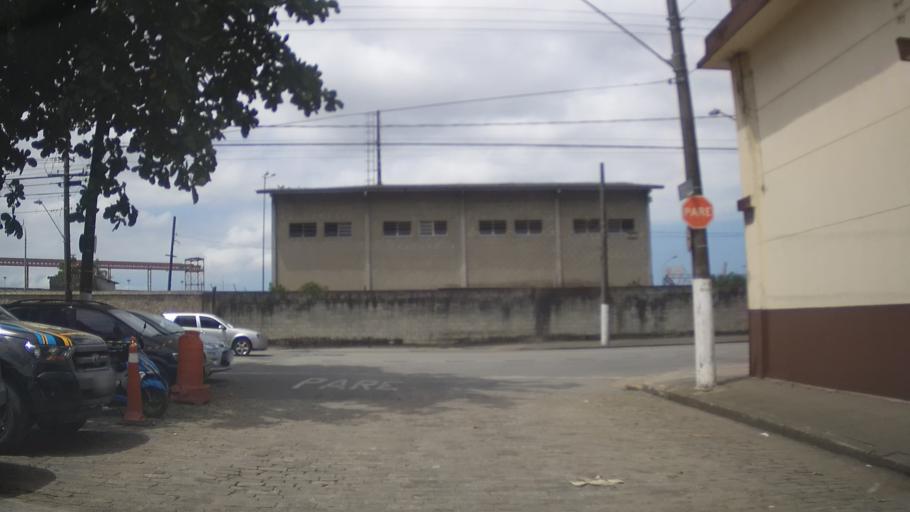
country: BR
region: Sao Paulo
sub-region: Santos
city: Santos
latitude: -23.9580
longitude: -46.3091
